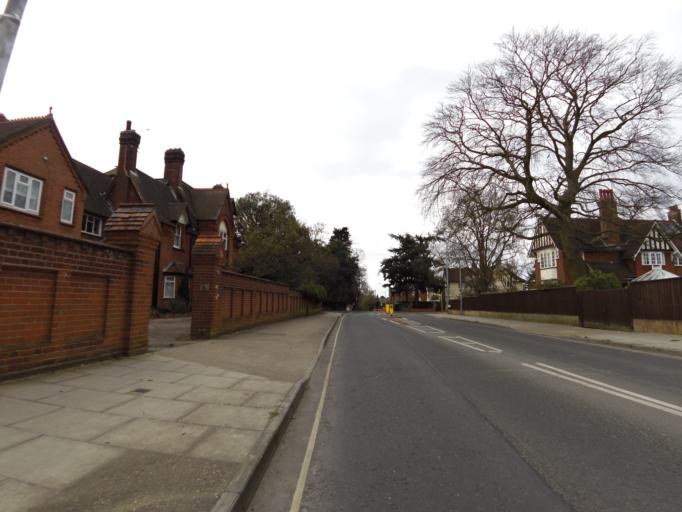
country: GB
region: England
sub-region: Suffolk
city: Ipswich
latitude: 52.0684
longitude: 1.1535
